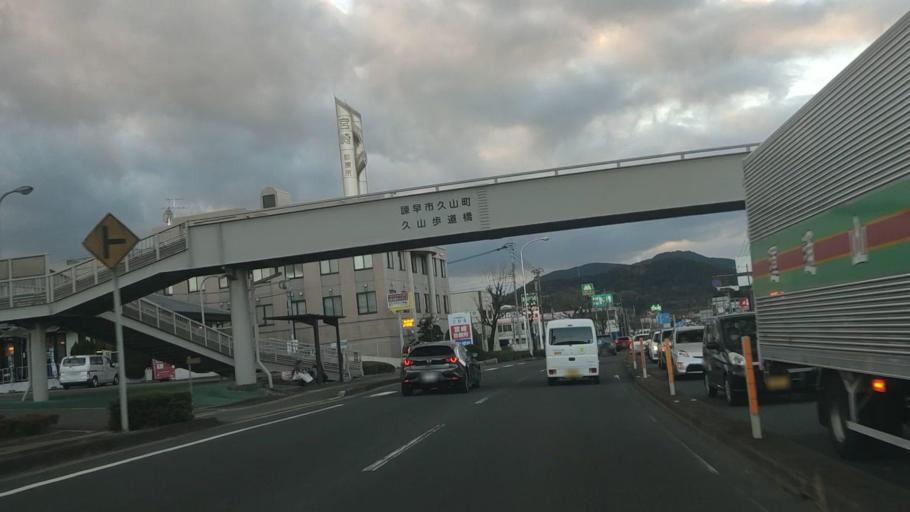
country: JP
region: Nagasaki
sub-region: Isahaya-shi
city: Isahaya
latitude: 32.8289
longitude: 129.9963
